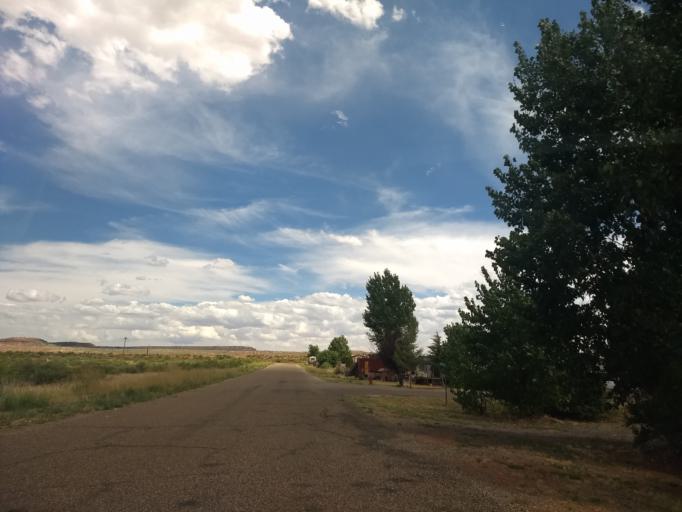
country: US
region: Arizona
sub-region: Coconino County
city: Fredonia
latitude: 36.9614
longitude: -112.5251
